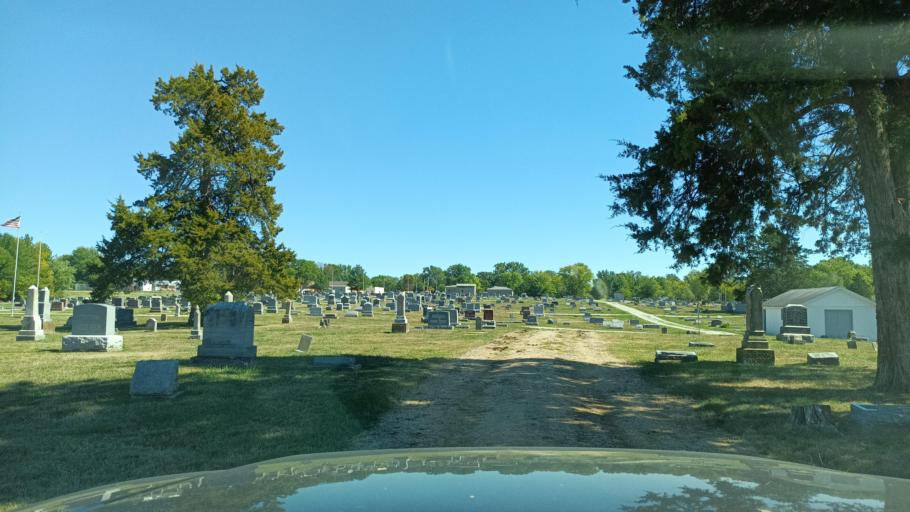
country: US
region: Missouri
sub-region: Macon County
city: La Plata
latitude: 40.0219
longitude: -92.5003
